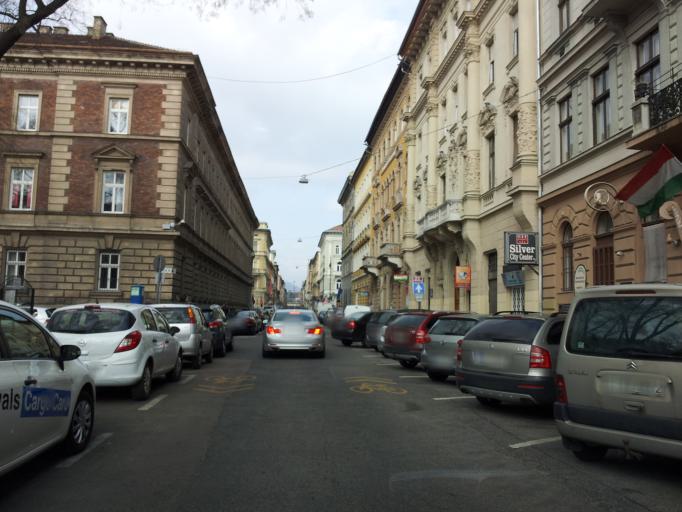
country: HU
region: Budapest
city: Budapest VI. keruelet
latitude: 47.5063
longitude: 19.0673
